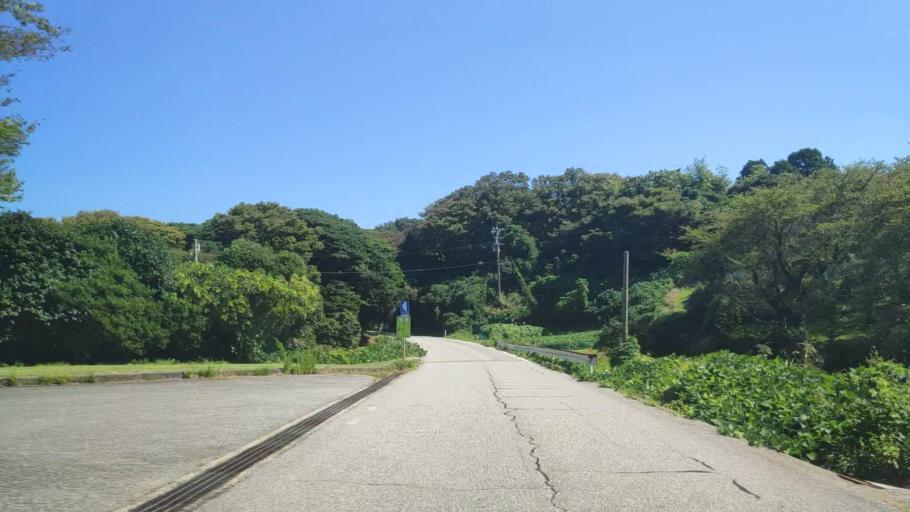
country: JP
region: Ishikawa
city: Nanao
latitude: 37.5255
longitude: 137.2625
